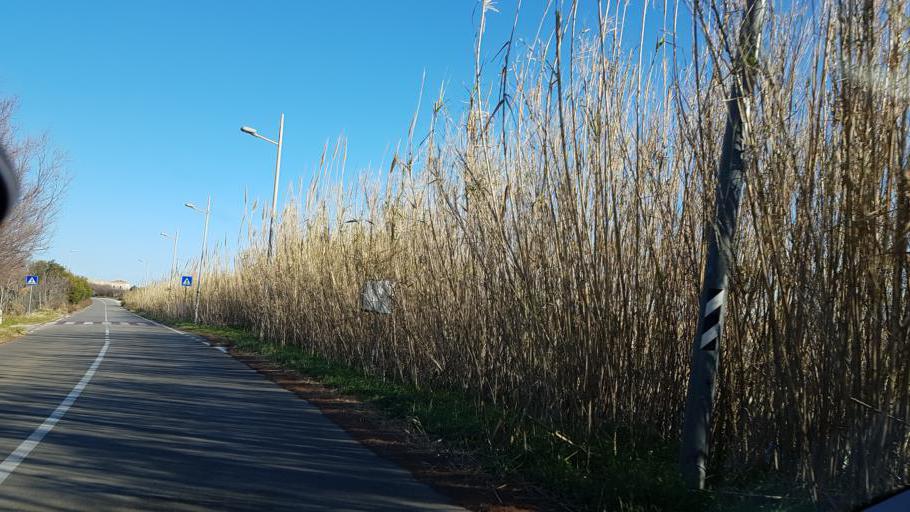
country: IT
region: Apulia
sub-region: Provincia di Brindisi
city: Brindisi
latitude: 40.6809
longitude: 17.8927
